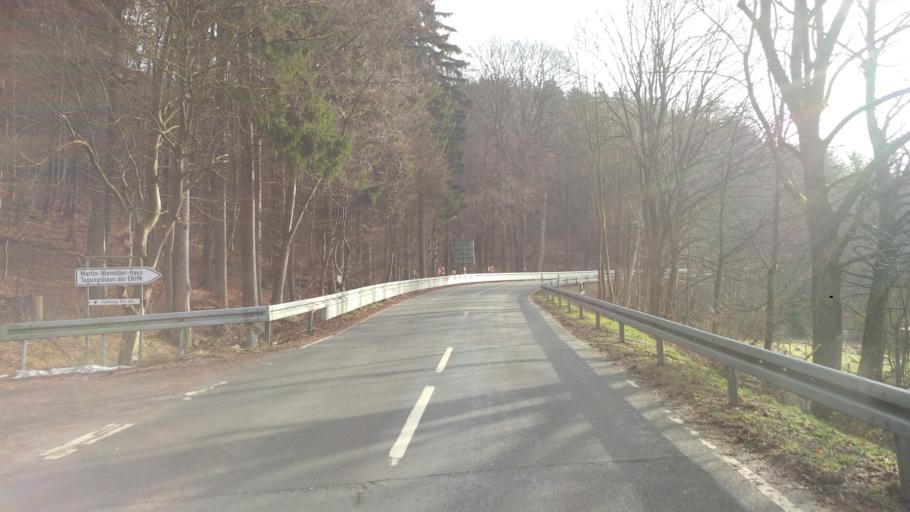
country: DE
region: Hesse
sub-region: Regierungsbezirk Darmstadt
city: Schmitten
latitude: 50.2650
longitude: 8.4597
